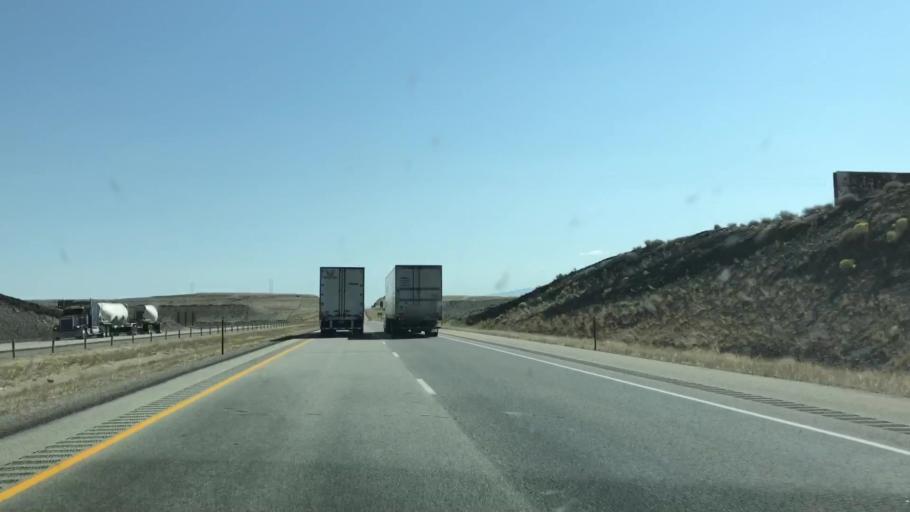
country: US
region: Wyoming
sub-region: Carbon County
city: Rawlins
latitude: 41.7828
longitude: -107.1612
